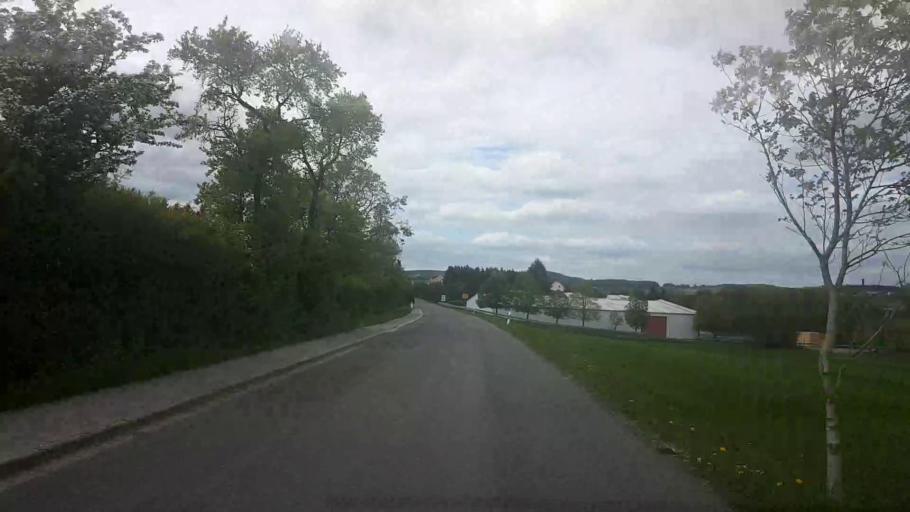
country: DE
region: Bavaria
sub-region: Upper Franconia
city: Untersiemau
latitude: 50.2020
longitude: 10.9818
